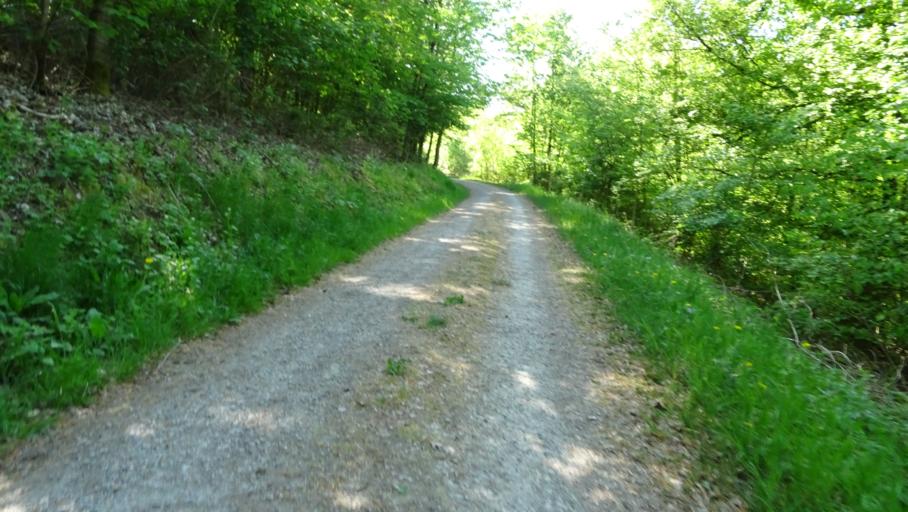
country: DE
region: Baden-Wuerttemberg
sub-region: Karlsruhe Region
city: Mosbach
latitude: 49.3460
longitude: 9.1531
